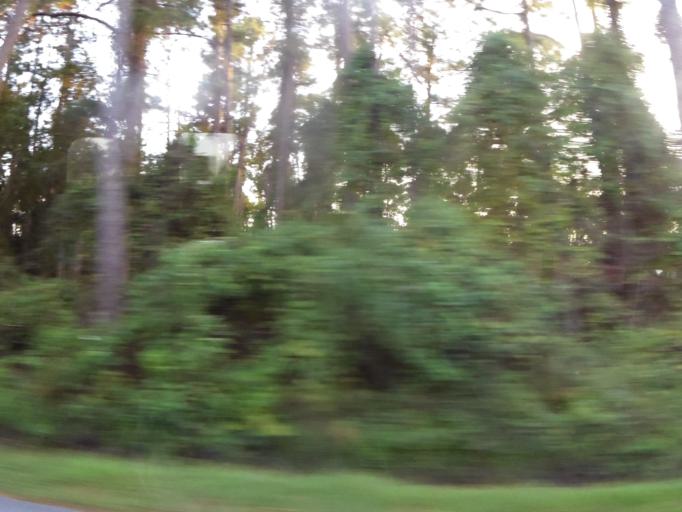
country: US
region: Florida
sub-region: Saint Johns County
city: Fruit Cove
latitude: 30.1815
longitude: -81.6315
